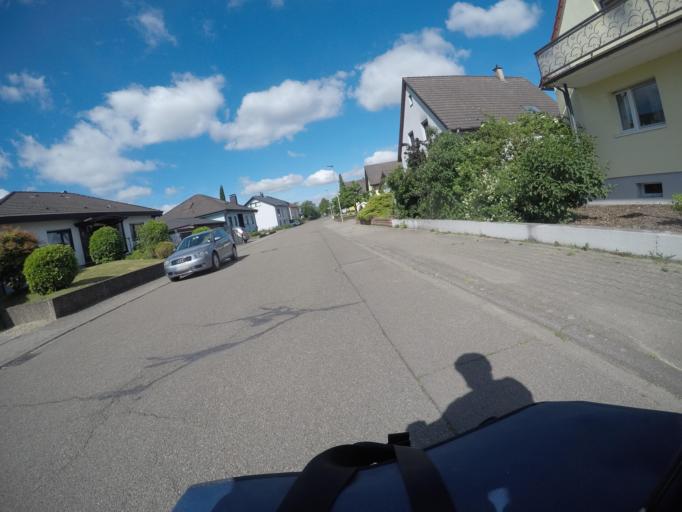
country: DE
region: Baden-Wuerttemberg
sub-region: Karlsruhe Region
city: Au am Rhein
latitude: 48.9486
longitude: 8.2344
